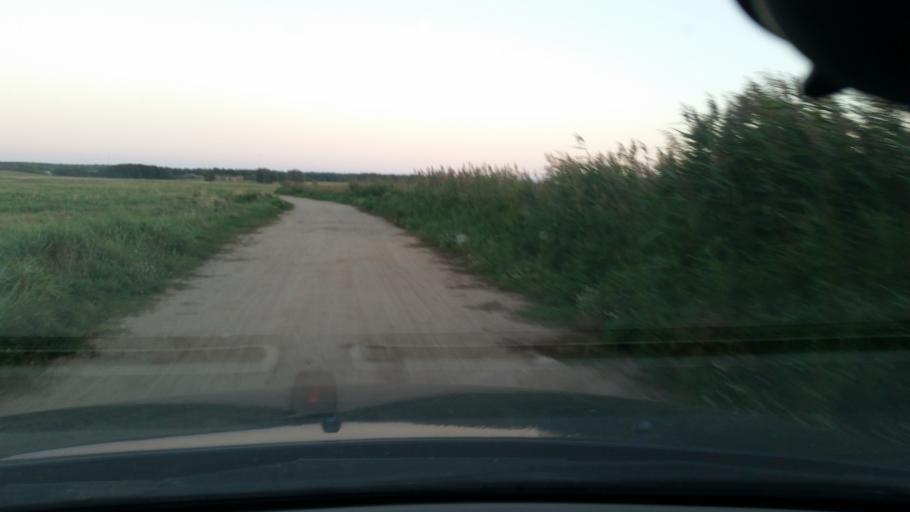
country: PL
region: Pomeranian Voivodeship
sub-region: Powiat wejherowski
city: Choczewo
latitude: 54.7885
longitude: 17.7940
